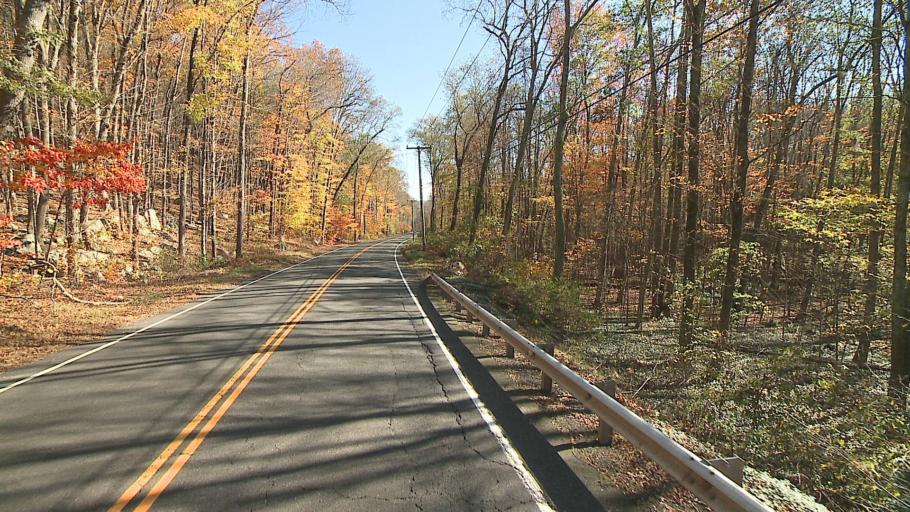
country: US
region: Connecticut
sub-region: Tolland County
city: Coventry Lake
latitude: 41.7982
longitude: -72.3294
